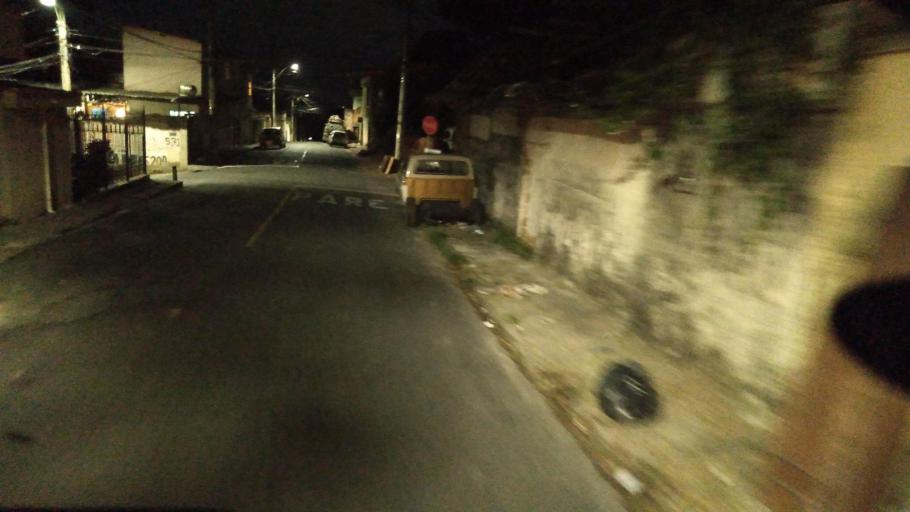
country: BR
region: Minas Gerais
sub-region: Belo Horizonte
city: Belo Horizonte
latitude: -19.8877
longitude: -43.9612
